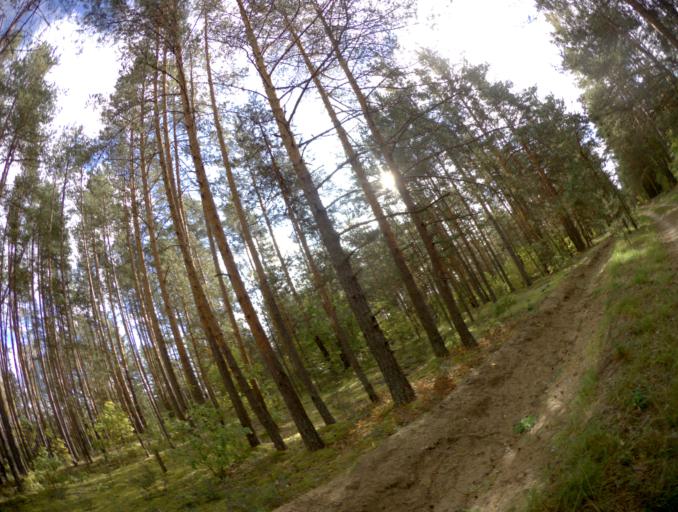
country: RU
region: Vladimir
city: Petushki
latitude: 55.8857
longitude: 39.4964
